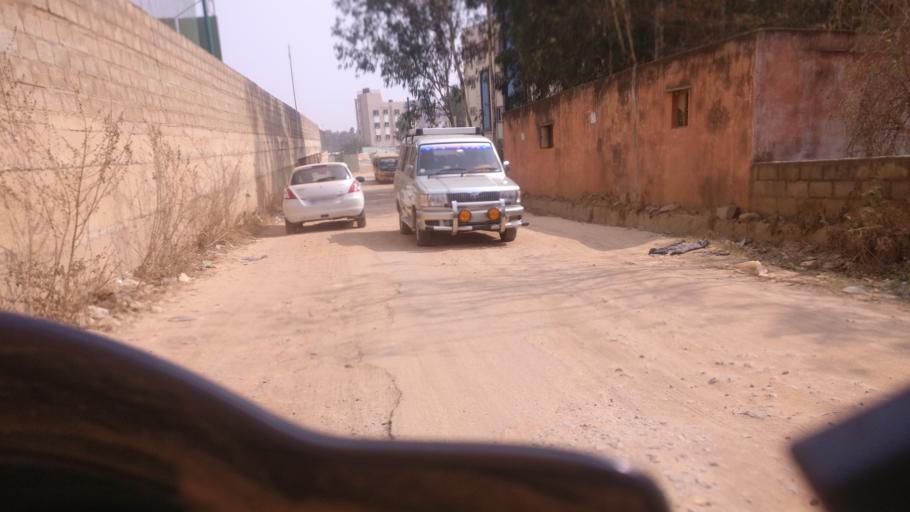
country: IN
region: Karnataka
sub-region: Bangalore Urban
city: Bangalore
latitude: 12.8952
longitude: 77.6780
